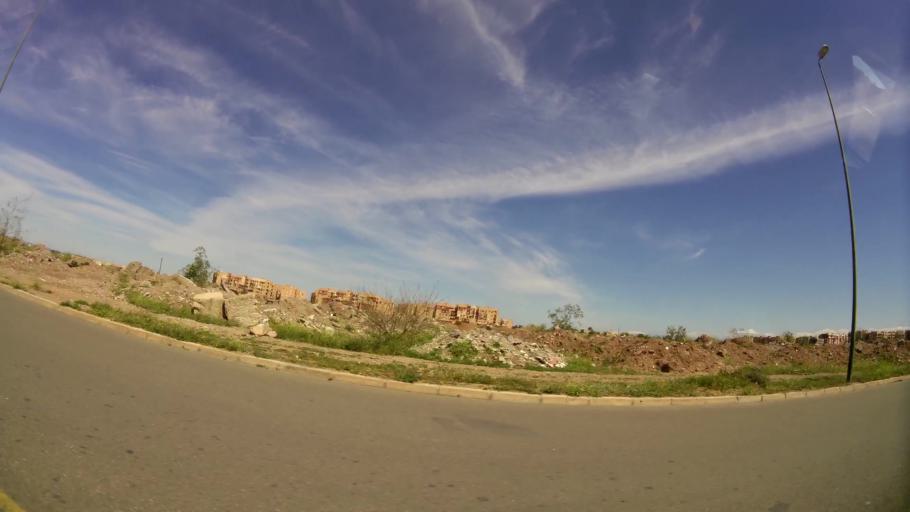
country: MA
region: Marrakech-Tensift-Al Haouz
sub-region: Marrakech
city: Marrakesh
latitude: 31.6468
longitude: -8.0791
